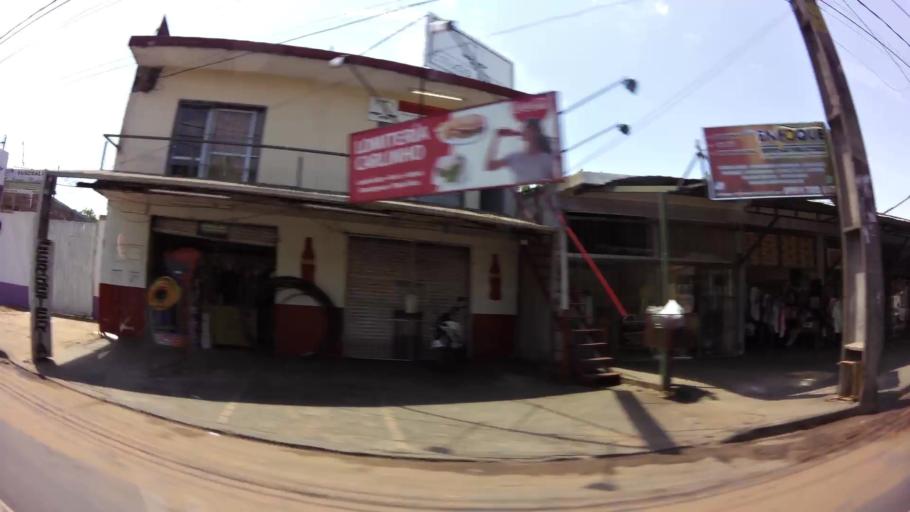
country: PY
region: Central
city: Nemby
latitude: -25.3854
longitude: -57.5492
